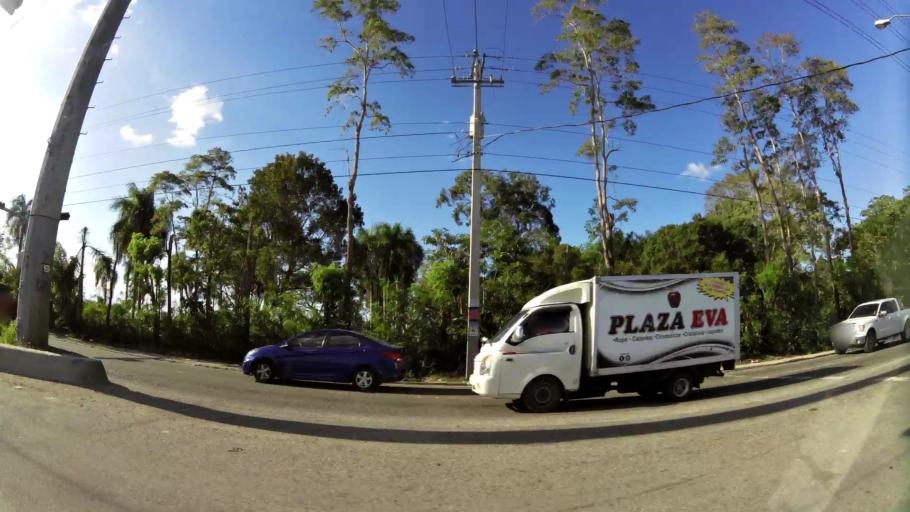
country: DO
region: Nacional
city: Santo Domingo
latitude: 18.5088
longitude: -69.9679
